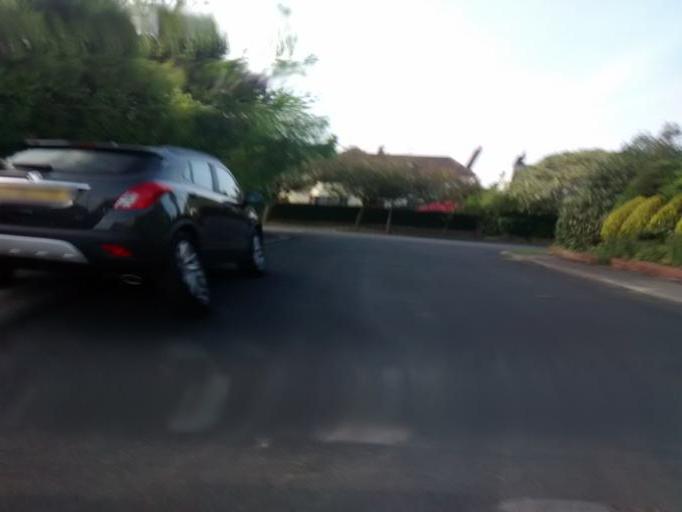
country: GB
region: England
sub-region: County Durham
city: Durham
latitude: 54.7559
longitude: -1.5903
